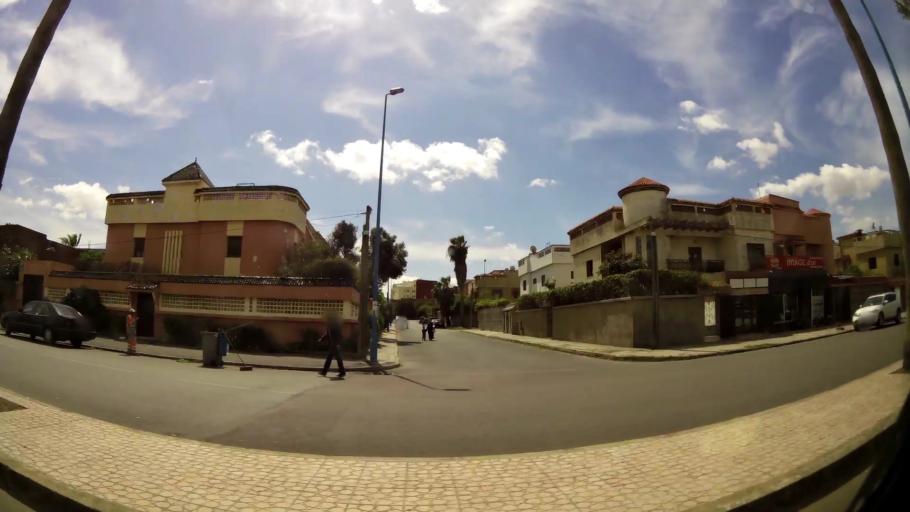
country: MA
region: Grand Casablanca
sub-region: Mediouna
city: Tit Mellil
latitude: 33.6146
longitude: -7.5326
